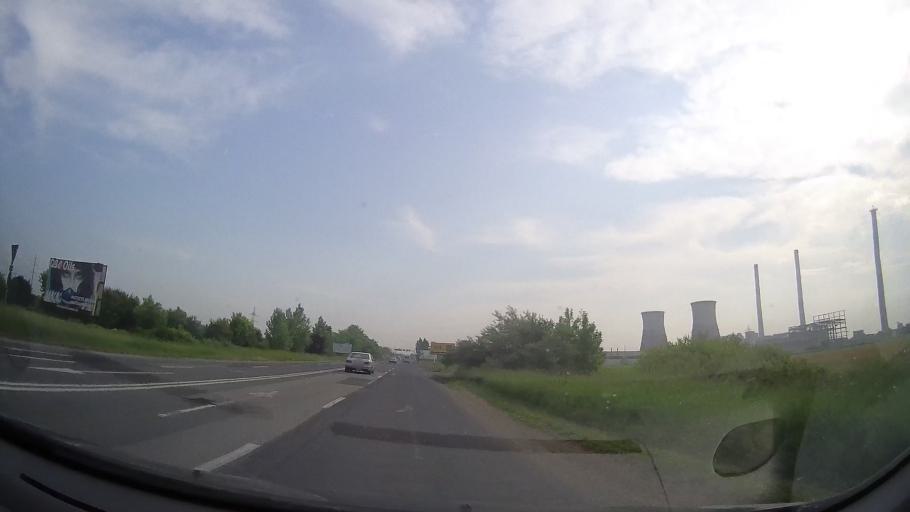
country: RO
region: Timis
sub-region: Comuna Giroc
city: Chisoda
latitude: 45.7073
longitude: 21.1879
